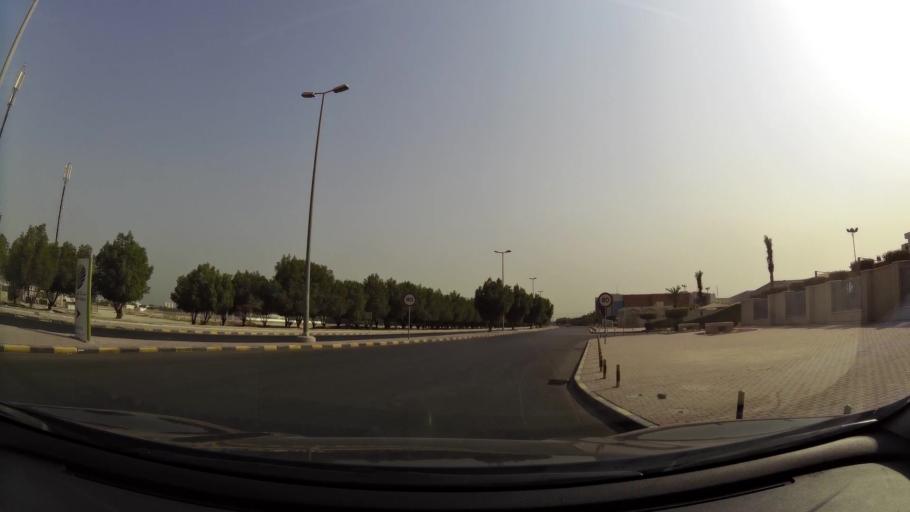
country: KW
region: Mubarak al Kabir
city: Sabah as Salim
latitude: 29.2768
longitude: 48.0536
